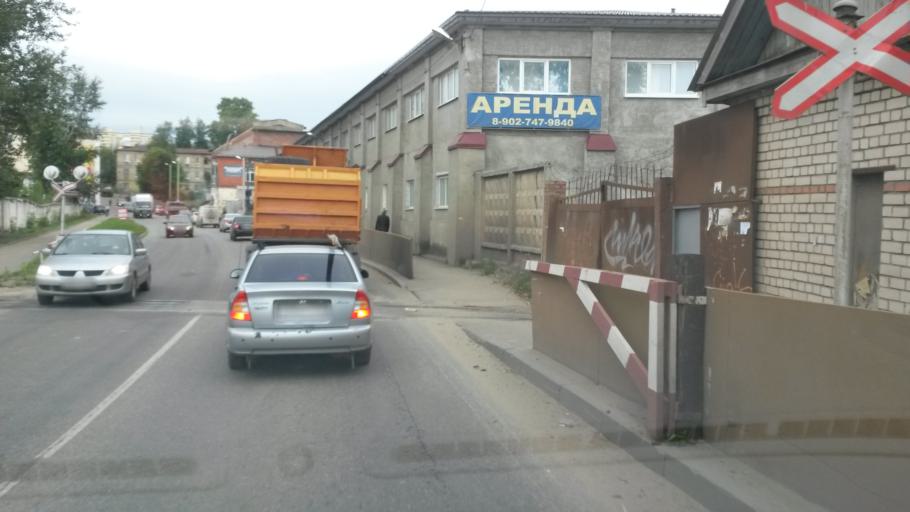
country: RU
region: Ivanovo
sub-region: Gorod Ivanovo
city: Ivanovo
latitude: 57.0132
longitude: 40.9536
